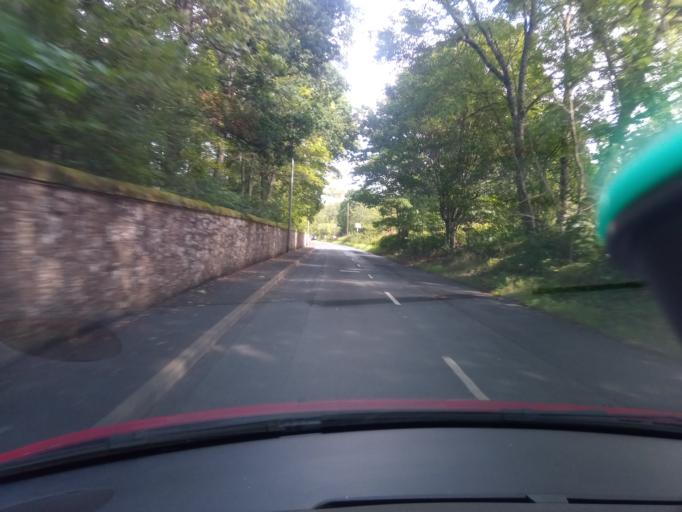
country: GB
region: Scotland
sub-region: The Scottish Borders
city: Melrose
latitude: 55.5886
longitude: -2.7286
